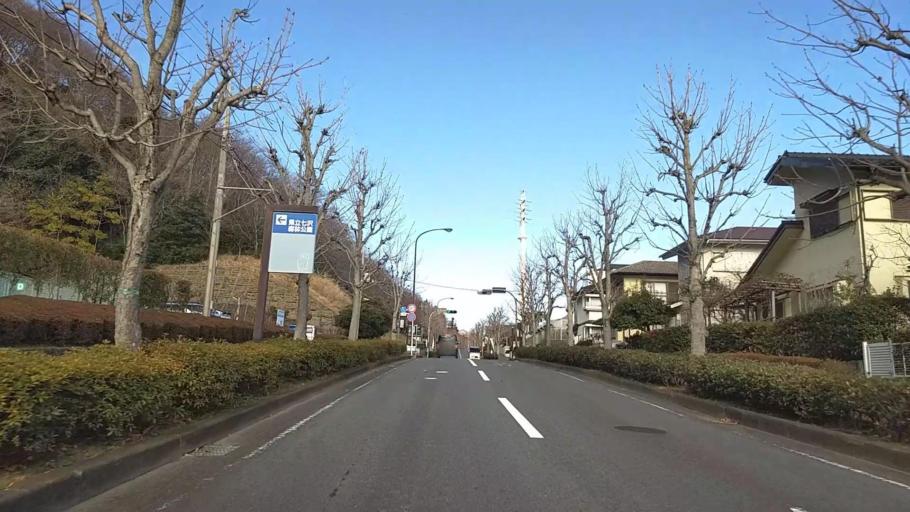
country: JP
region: Kanagawa
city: Atsugi
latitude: 35.4470
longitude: 139.3046
